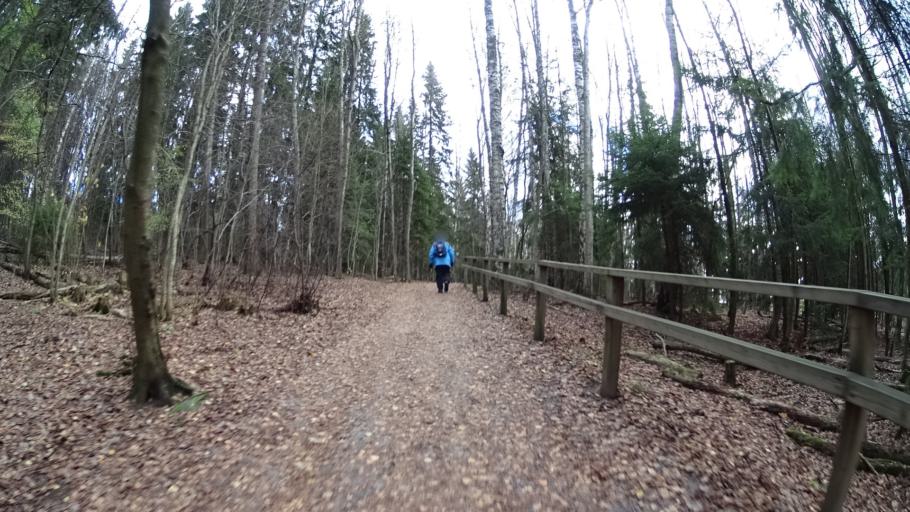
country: FI
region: Uusimaa
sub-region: Helsinki
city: Teekkarikylae
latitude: 60.2611
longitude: 24.8633
